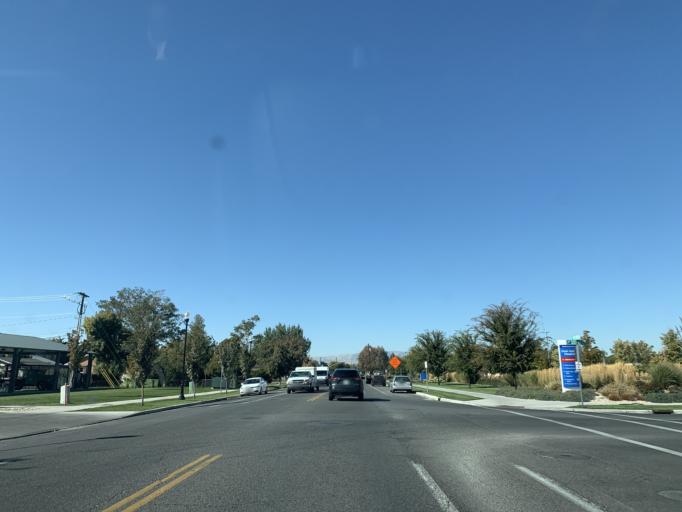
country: US
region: Utah
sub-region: Utah County
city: Provo
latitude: 40.2443
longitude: -111.6639
